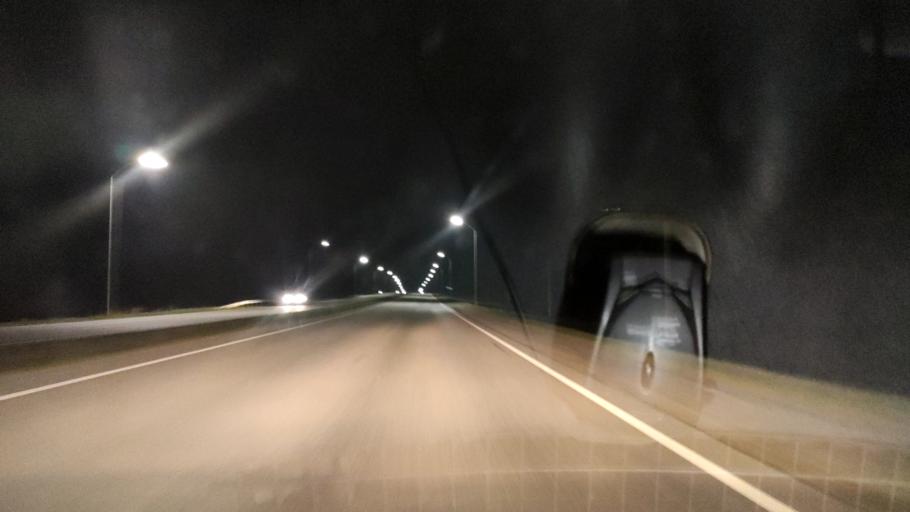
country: RU
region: Belgorod
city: Staryy Oskol
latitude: 51.3831
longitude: 37.8574
